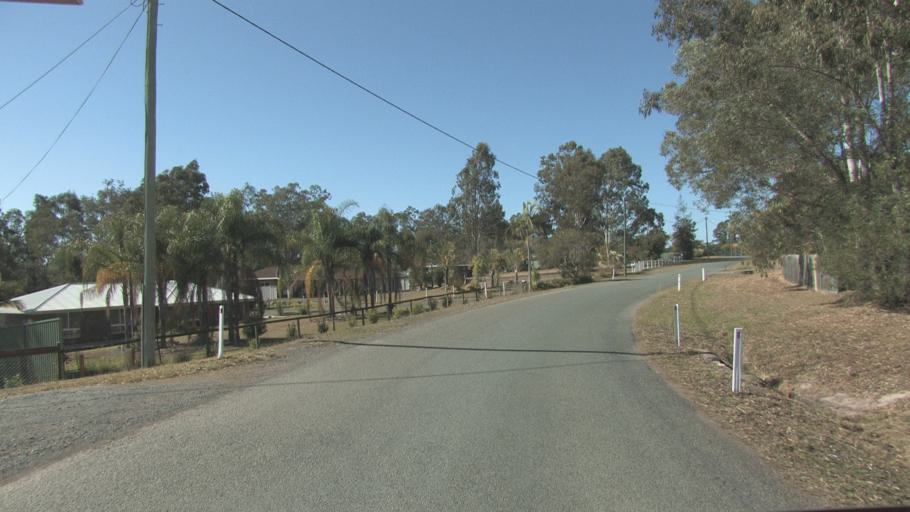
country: AU
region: Queensland
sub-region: Logan
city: Cedar Vale
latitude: -27.8523
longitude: 153.0173
